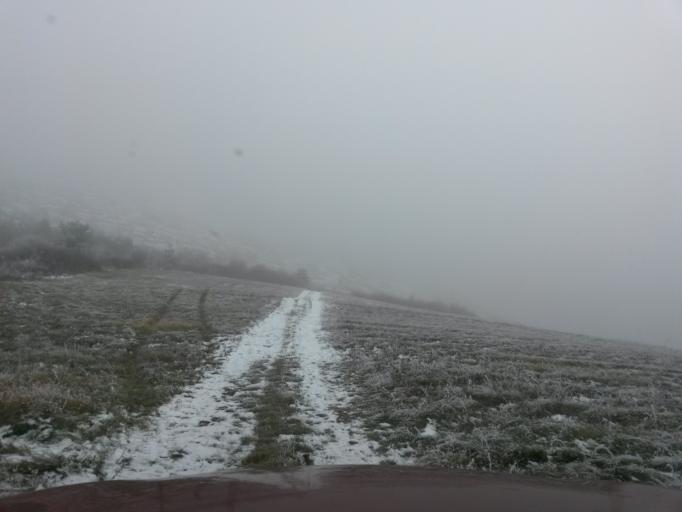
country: SK
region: Kosicky
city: Krompachy
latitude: 48.9701
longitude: 20.9782
